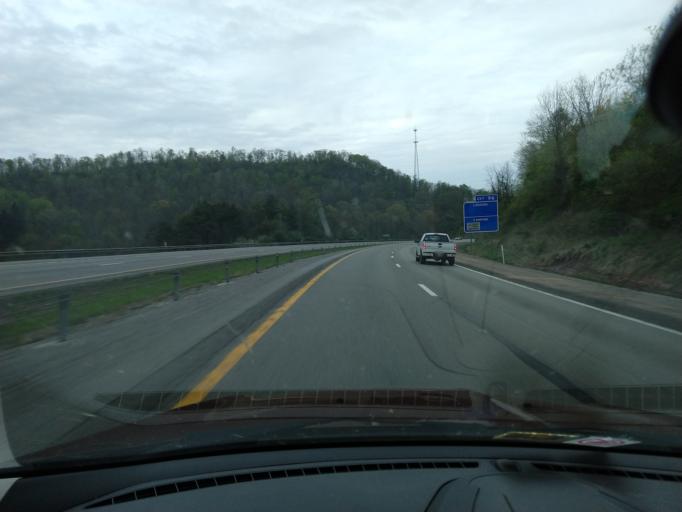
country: US
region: West Virginia
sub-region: Lewis County
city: Weston
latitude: 39.0127
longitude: -80.4934
